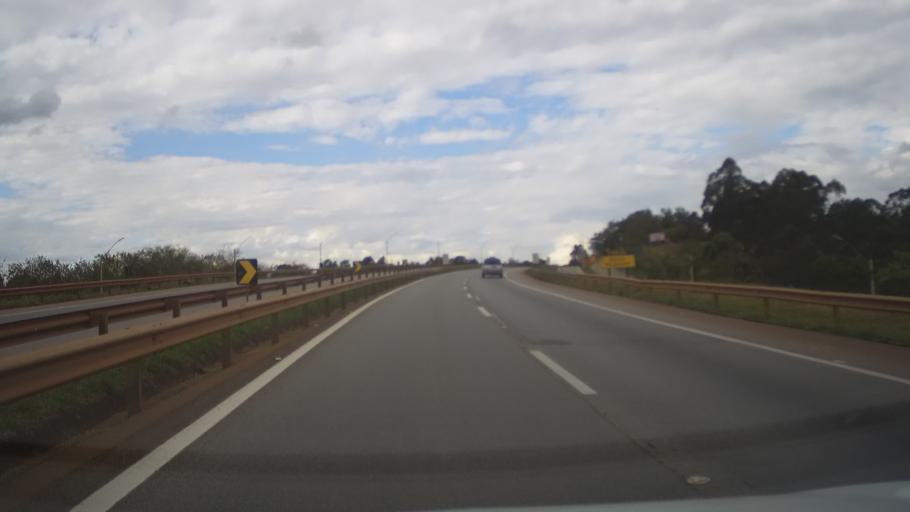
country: BR
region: Minas Gerais
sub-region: Itauna
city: Itauna
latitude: -20.3049
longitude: -44.4466
